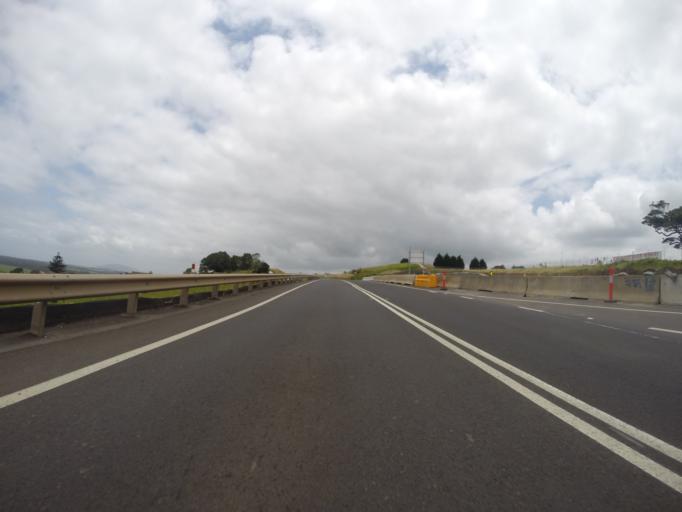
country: AU
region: New South Wales
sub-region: Kiama
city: Gerringong
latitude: -34.7457
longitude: 150.8094
